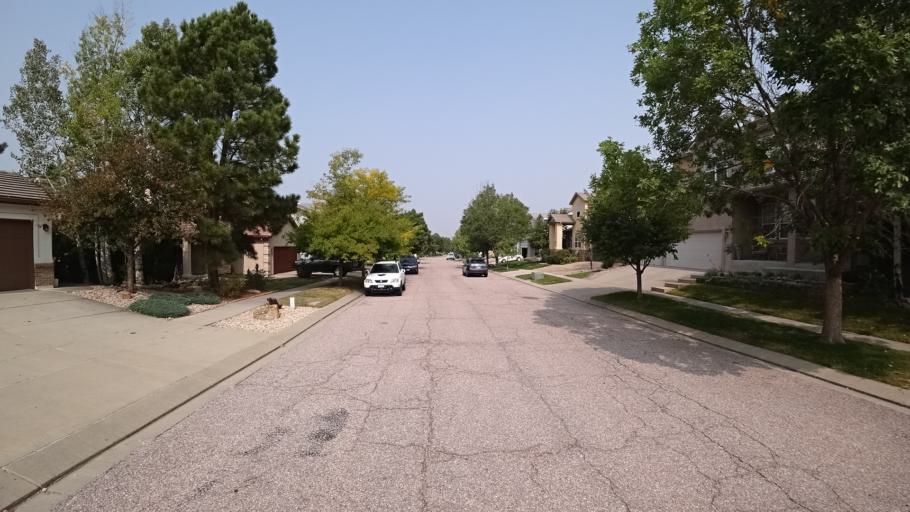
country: US
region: Colorado
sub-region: El Paso County
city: Cimarron Hills
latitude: 38.9166
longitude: -104.7420
